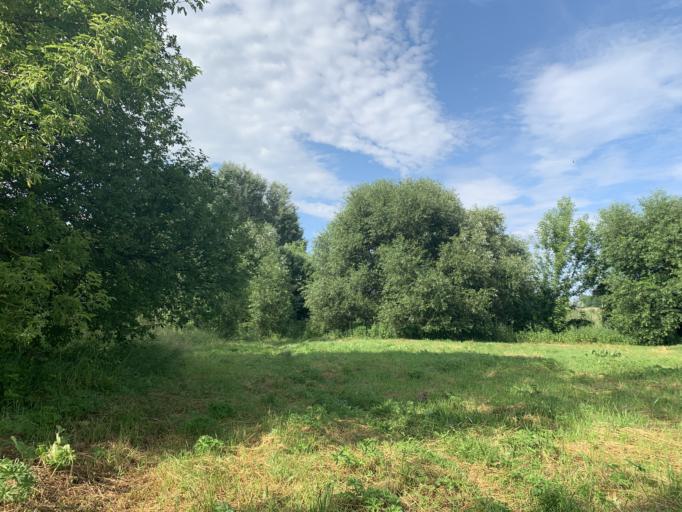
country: BY
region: Minsk
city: Nyasvizh
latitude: 53.2153
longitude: 26.6837
